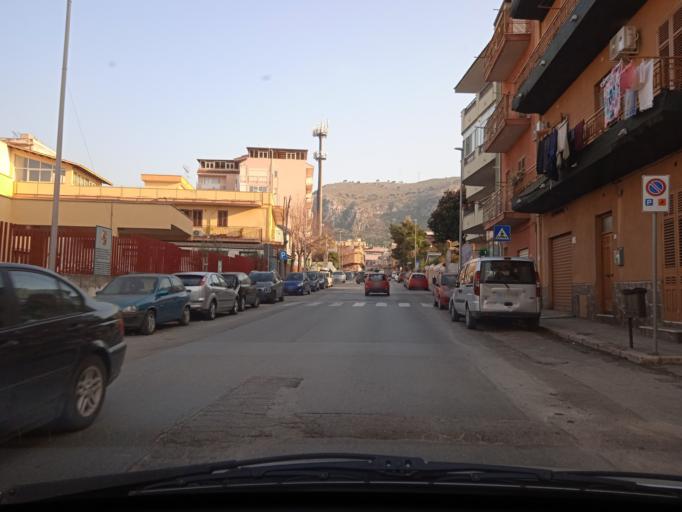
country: IT
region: Sicily
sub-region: Palermo
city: Villabate
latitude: 38.0782
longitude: 13.4380
